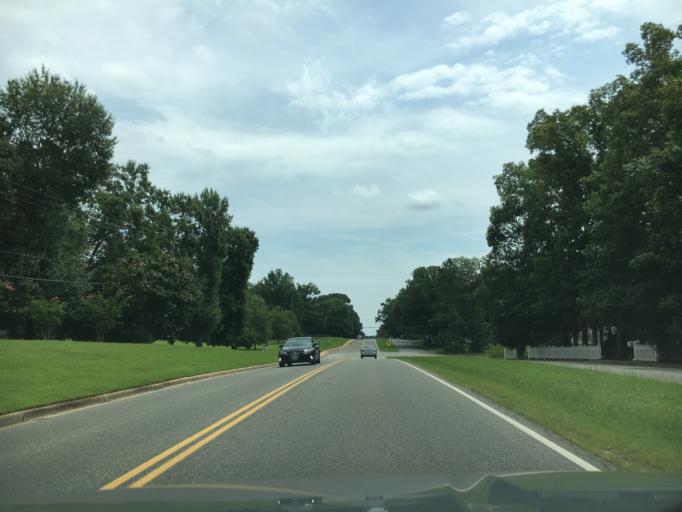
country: US
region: Virginia
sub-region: Henrico County
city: Short Pump
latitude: 37.6066
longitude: -77.6292
